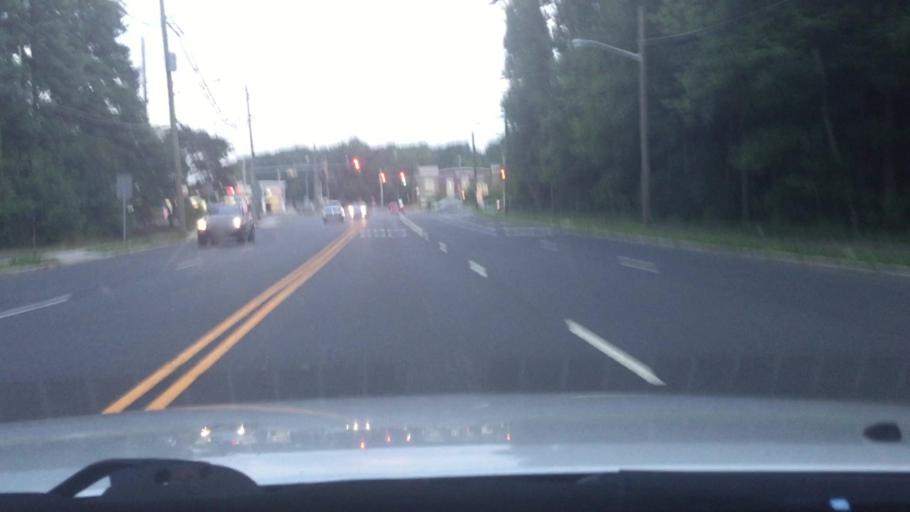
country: US
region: New Jersey
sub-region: Middlesex County
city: Milltown
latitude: 40.4409
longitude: -74.4791
